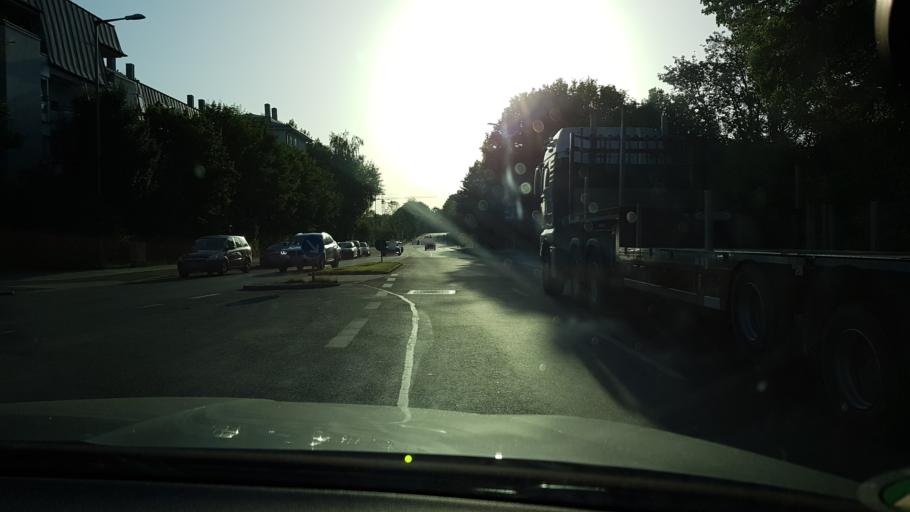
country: DE
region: Bavaria
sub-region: Upper Bavaria
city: Unterfoehring
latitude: 48.1687
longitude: 11.6374
